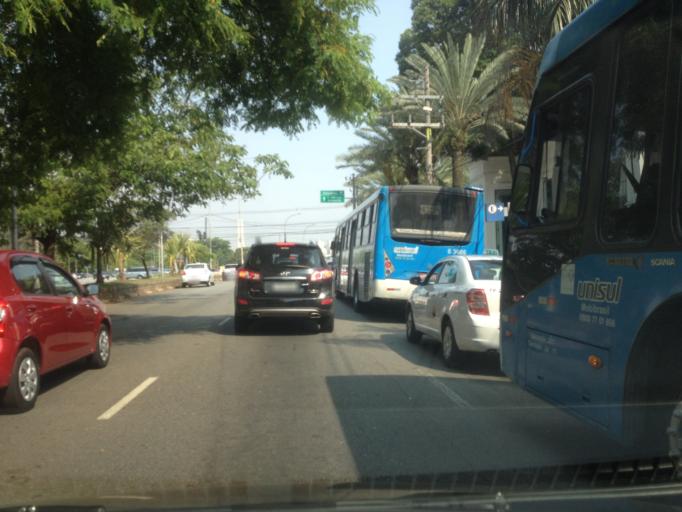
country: BR
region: Sao Paulo
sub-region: Sao Paulo
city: Sao Paulo
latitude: -23.5786
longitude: -46.6623
